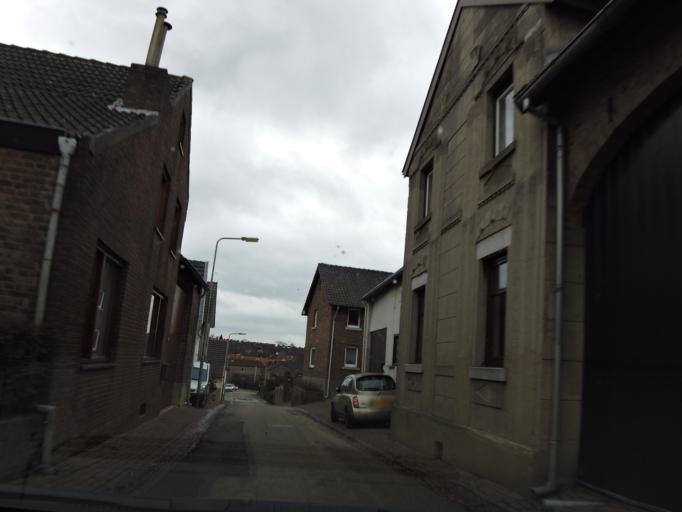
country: NL
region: Limburg
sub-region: Eijsden-Margraten
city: Margraten
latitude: 50.7934
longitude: 5.8060
